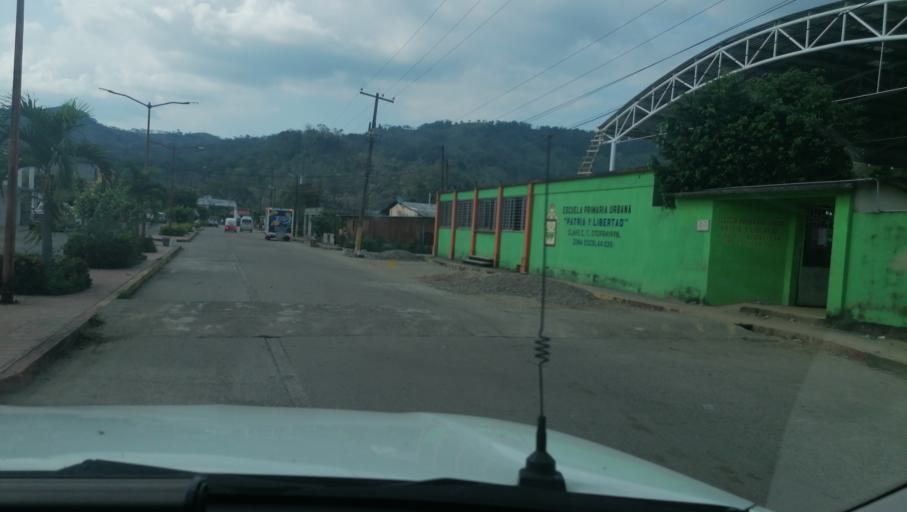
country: MX
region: Chiapas
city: Ostuacan
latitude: 17.4133
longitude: -93.3361
